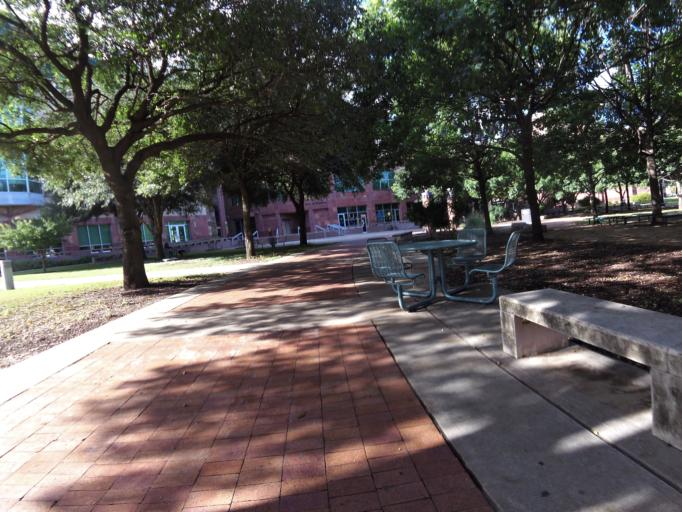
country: US
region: Texas
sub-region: Bexar County
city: San Antonio
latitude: 29.4235
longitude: -98.5031
